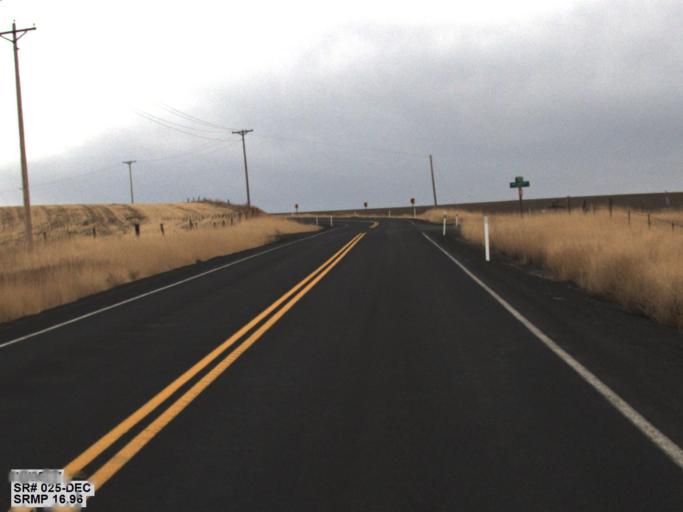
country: US
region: Washington
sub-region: Lincoln County
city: Davenport
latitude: 47.8618
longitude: -118.2441
